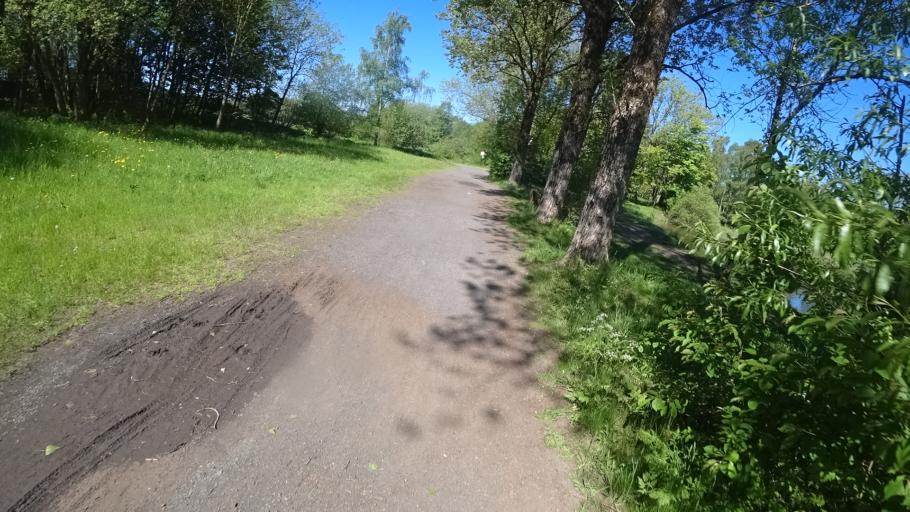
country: DE
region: Rheinland-Pfalz
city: Elkenroth
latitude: 50.7239
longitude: 7.9011
